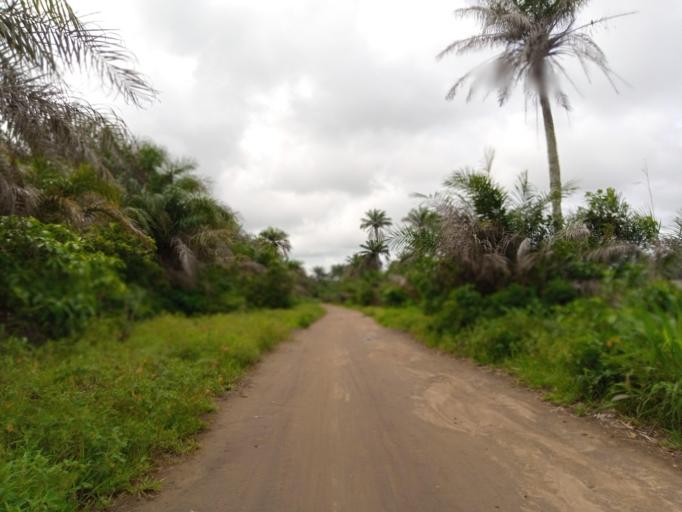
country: SL
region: Northern Province
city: Masoyila
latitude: 8.5852
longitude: -13.1946
